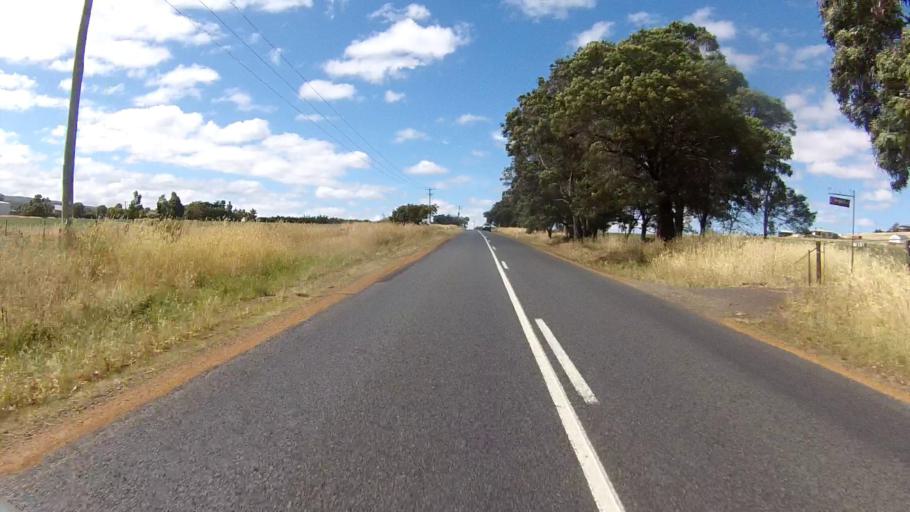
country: AU
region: Tasmania
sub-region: Sorell
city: Sorell
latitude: -42.6087
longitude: 147.4238
